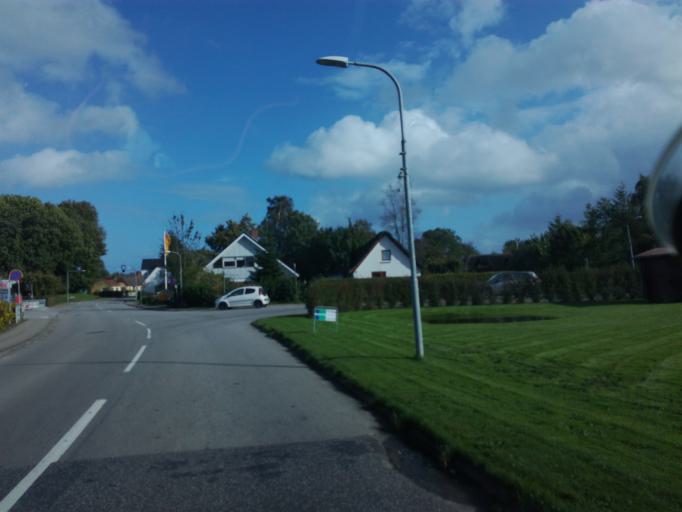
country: DK
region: South Denmark
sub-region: Vejle Kommune
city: Brejning
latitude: 55.6378
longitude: 9.6996
